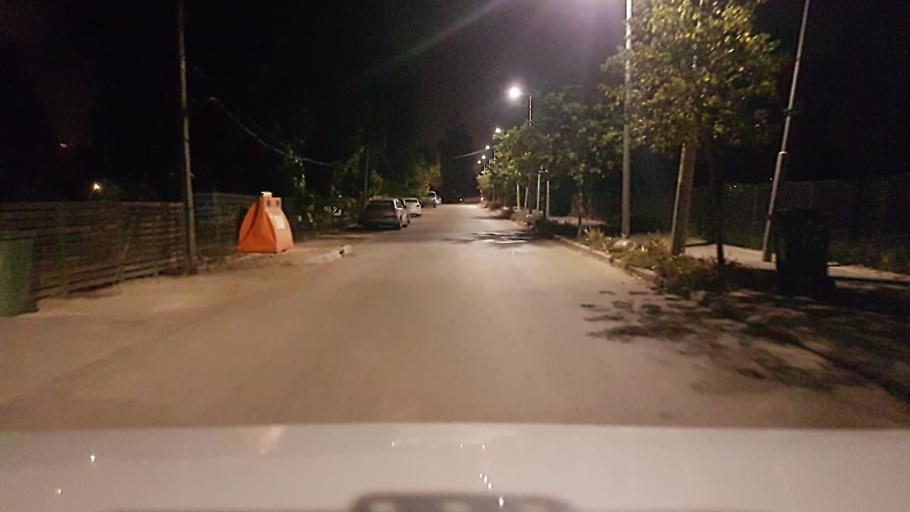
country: IL
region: Central District
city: Nehalim
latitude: 32.0748
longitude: 34.9302
